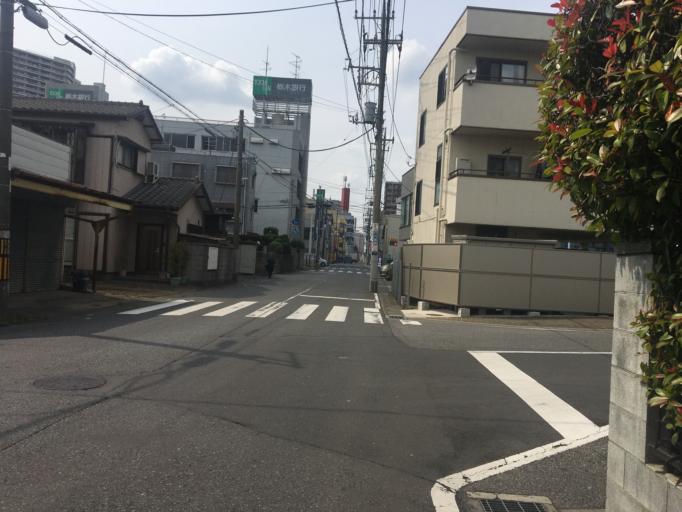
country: JP
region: Saitama
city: Koshigaya
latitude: 35.8875
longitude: 139.7908
